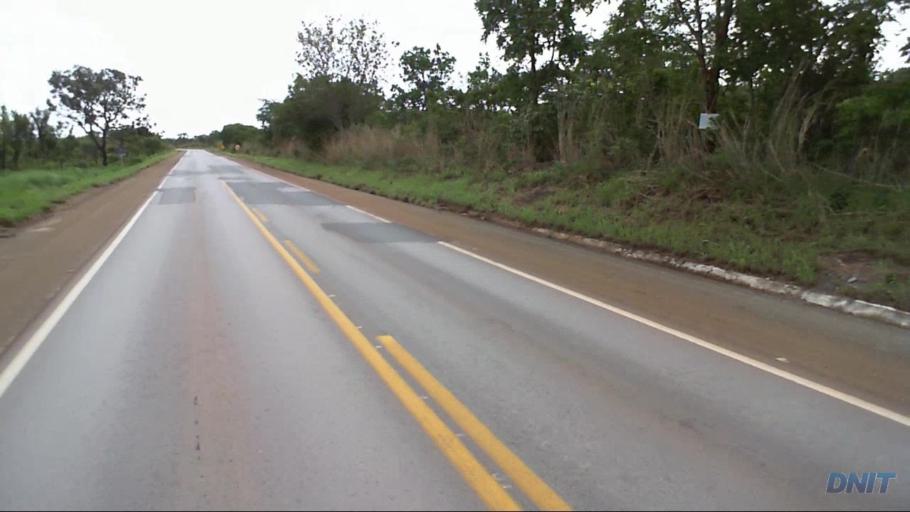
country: BR
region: Goias
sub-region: Barro Alto
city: Barro Alto
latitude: -14.7851
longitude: -49.0542
